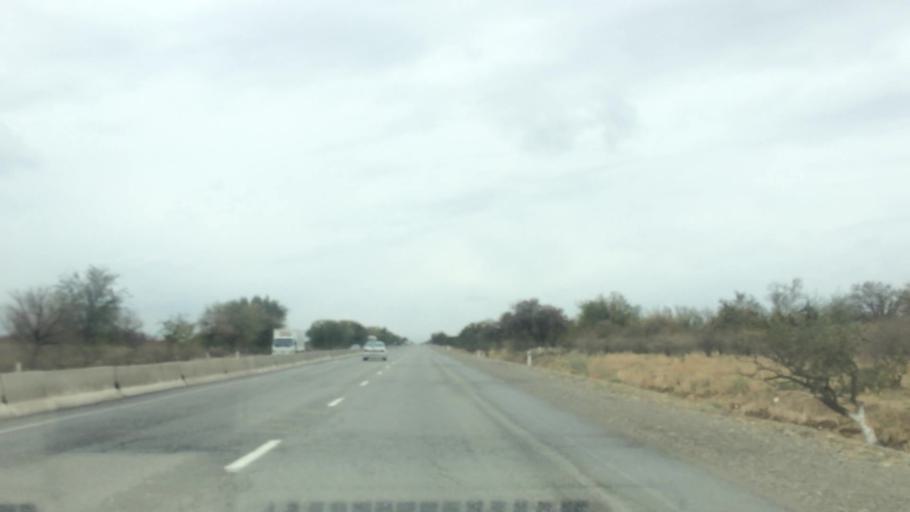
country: UZ
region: Samarqand
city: Bulung'ur
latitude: 39.8235
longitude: 67.3957
